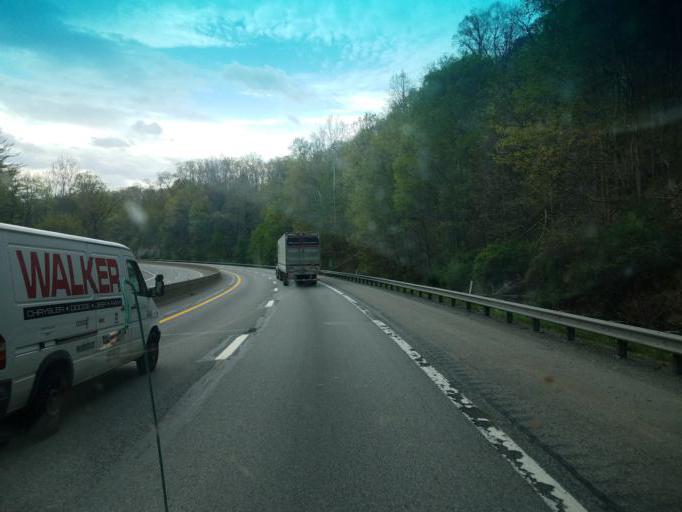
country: US
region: West Virginia
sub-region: Fayette County
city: Oak Hill
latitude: 37.9756
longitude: -81.2943
